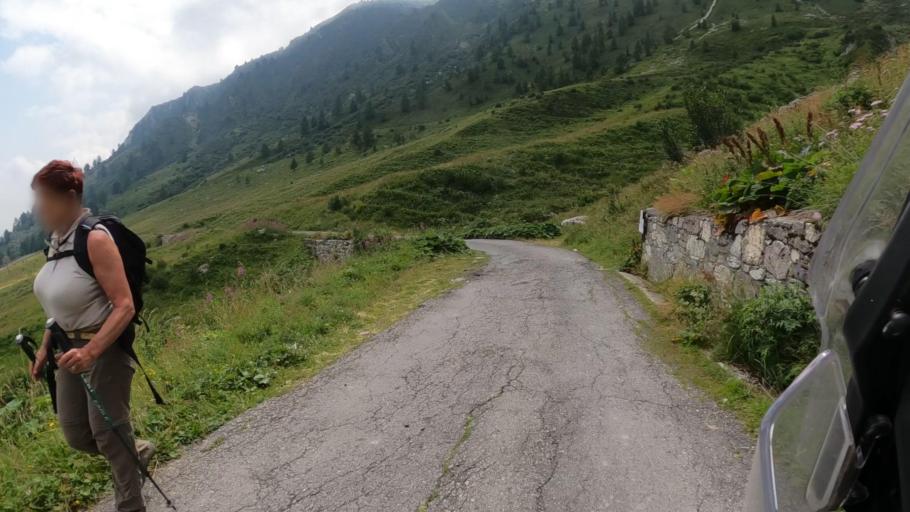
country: IT
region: Piedmont
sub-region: Provincia di Cuneo
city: Campomolino
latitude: 44.3906
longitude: 7.1493
